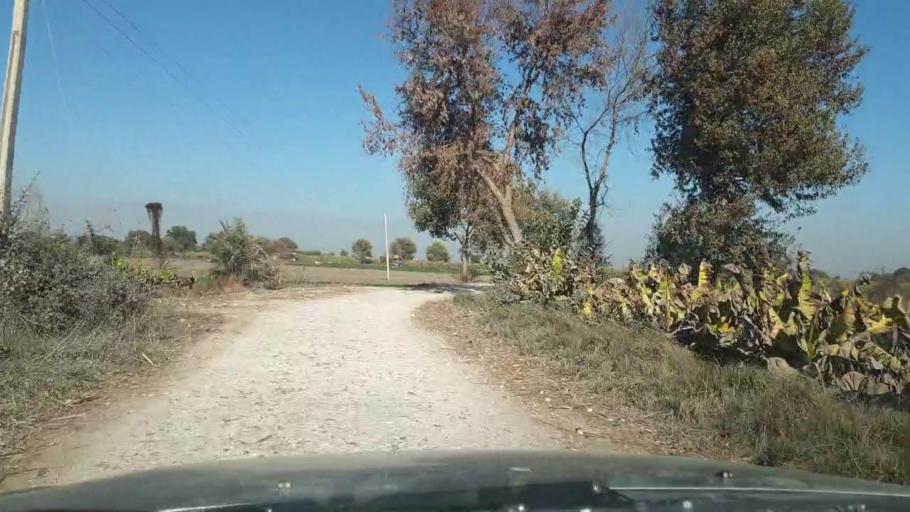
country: PK
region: Sindh
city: Ghotki
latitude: 28.0516
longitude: 69.2407
